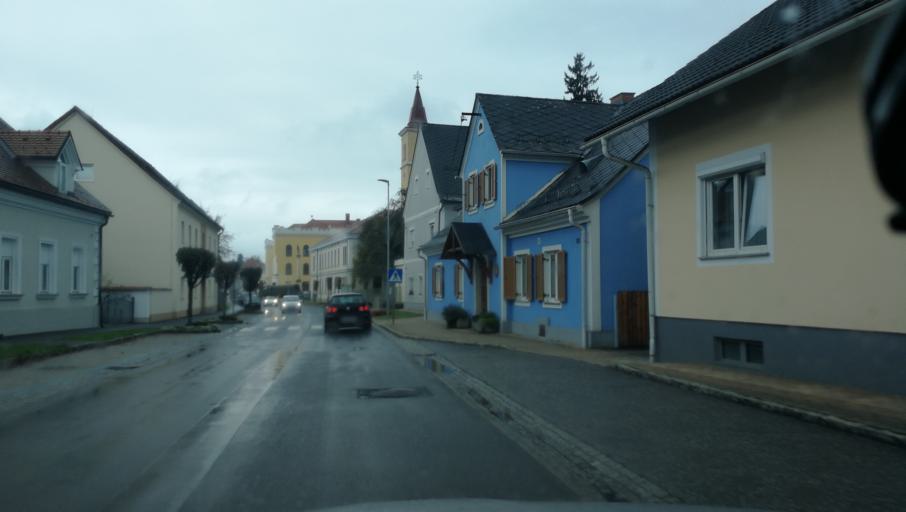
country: AT
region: Styria
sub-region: Politischer Bezirk Leibnitz
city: Strass in Steiermark
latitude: 46.7263
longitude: 15.6284
